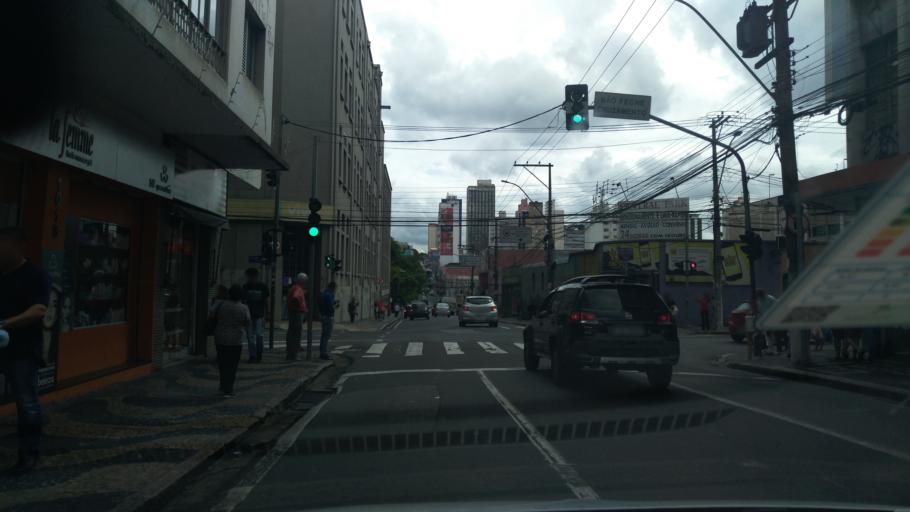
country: BR
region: Sao Paulo
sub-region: Campinas
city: Campinas
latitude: -22.9032
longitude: -47.0619
